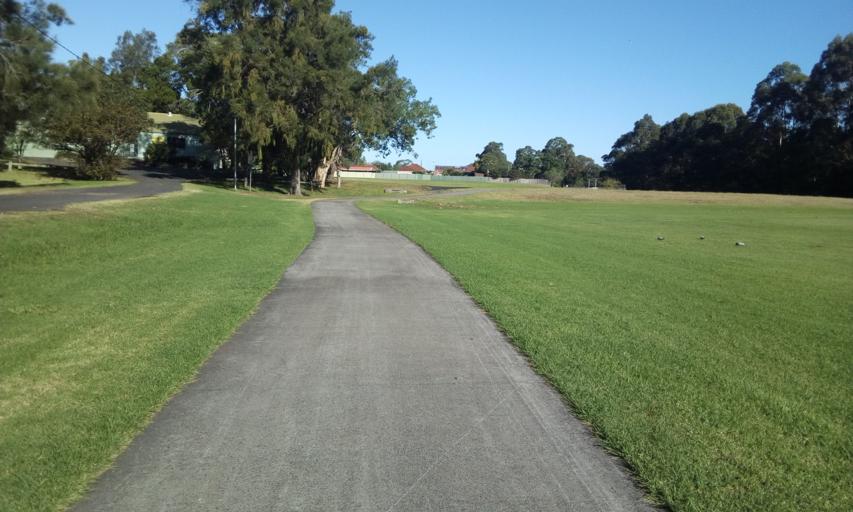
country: AU
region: New South Wales
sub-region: Wollongong
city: West Wollongong
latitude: -34.4245
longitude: 150.8612
